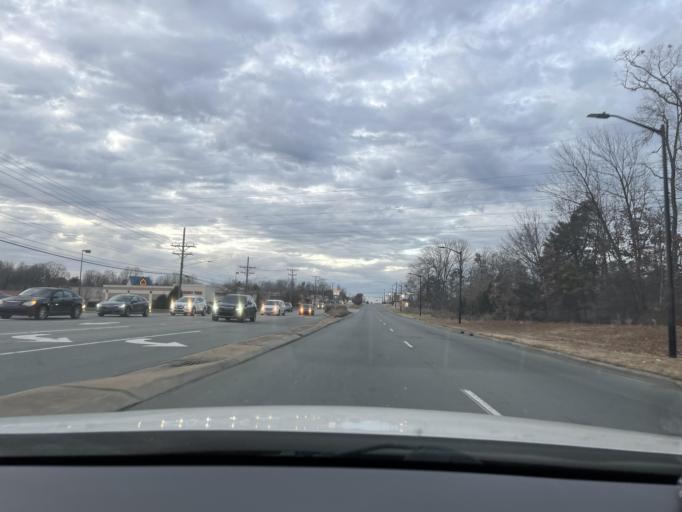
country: US
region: North Carolina
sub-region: Alamance County
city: Elon
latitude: 36.0687
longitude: -79.5201
